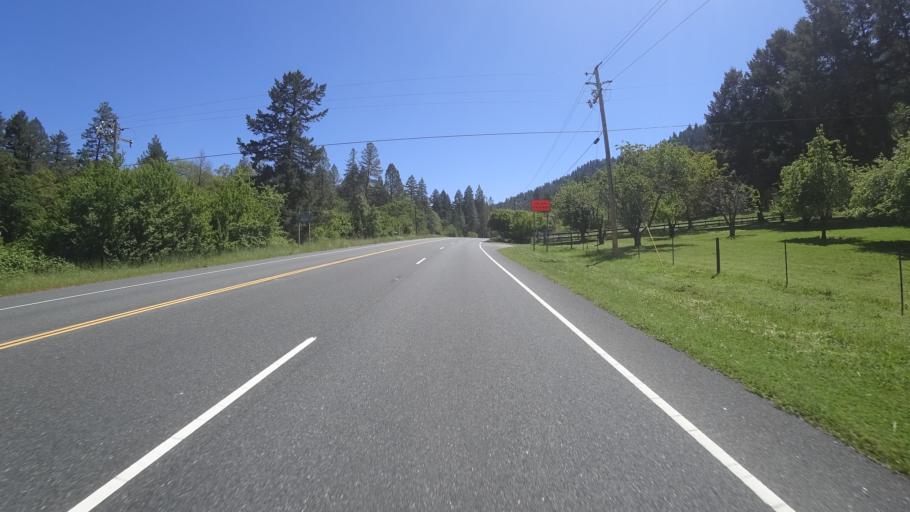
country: US
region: California
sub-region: Humboldt County
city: Willow Creek
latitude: 40.8793
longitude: -123.5404
